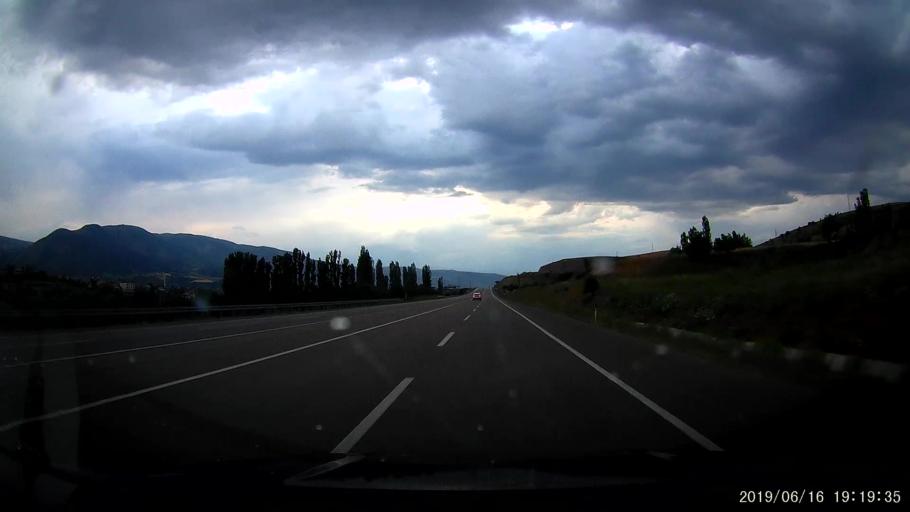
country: TR
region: Sivas
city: Akincilar
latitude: 40.0946
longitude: 38.4251
